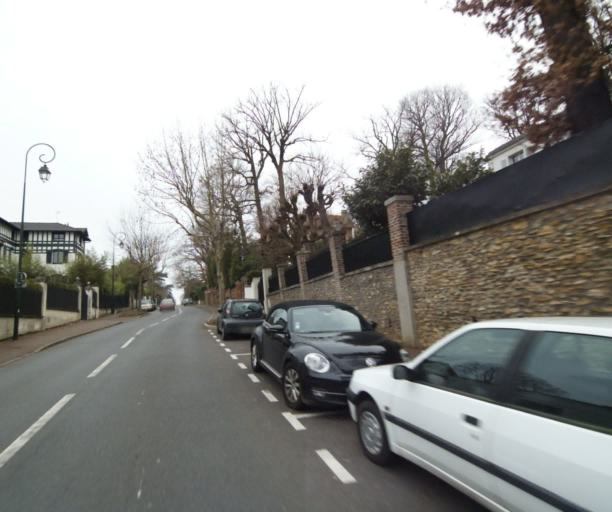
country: FR
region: Ile-de-France
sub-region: Departement des Hauts-de-Seine
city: Garches
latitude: 48.8428
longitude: 2.1768
